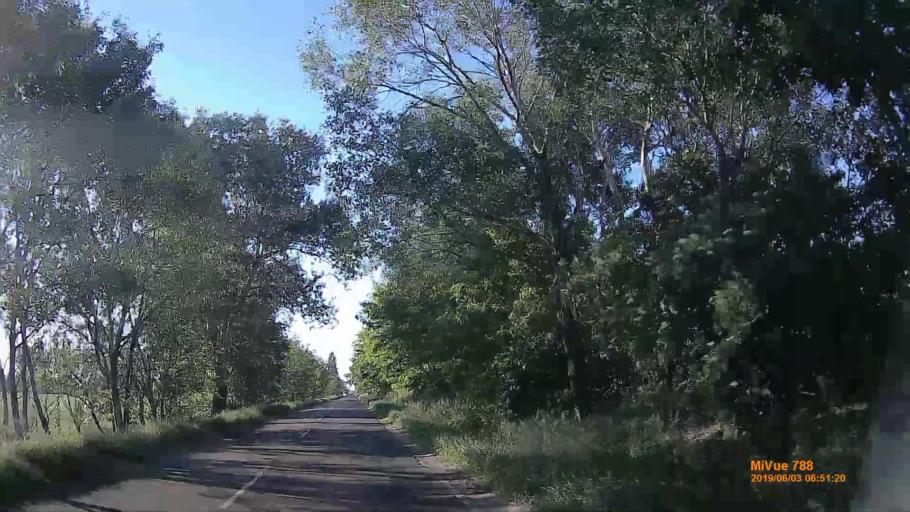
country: HU
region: Pest
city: Bugyi
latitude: 47.2121
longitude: 19.1832
